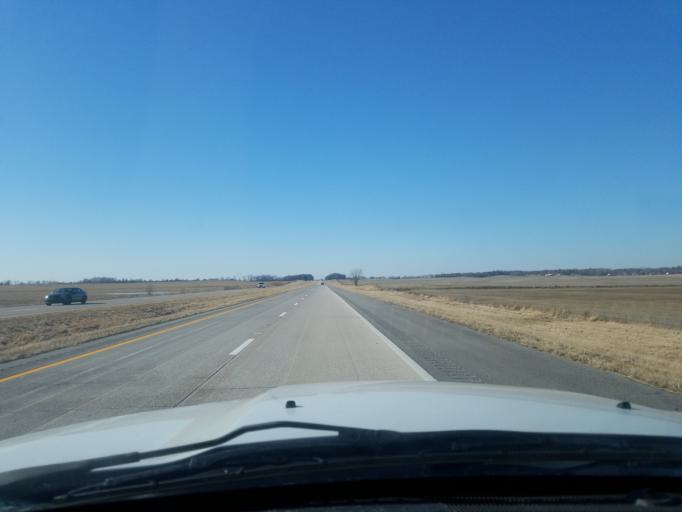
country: US
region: Kentucky
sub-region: Henderson County
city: Henderson
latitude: 37.8004
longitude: -87.5142
